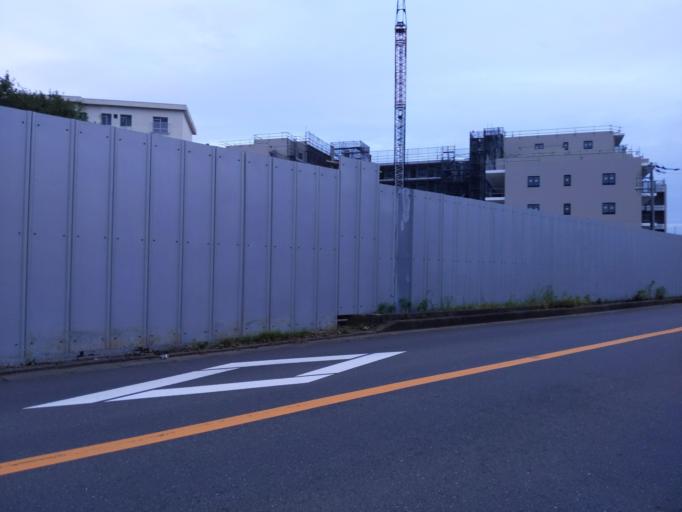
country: JP
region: Chiba
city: Funabashi
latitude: 35.7228
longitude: 139.9690
